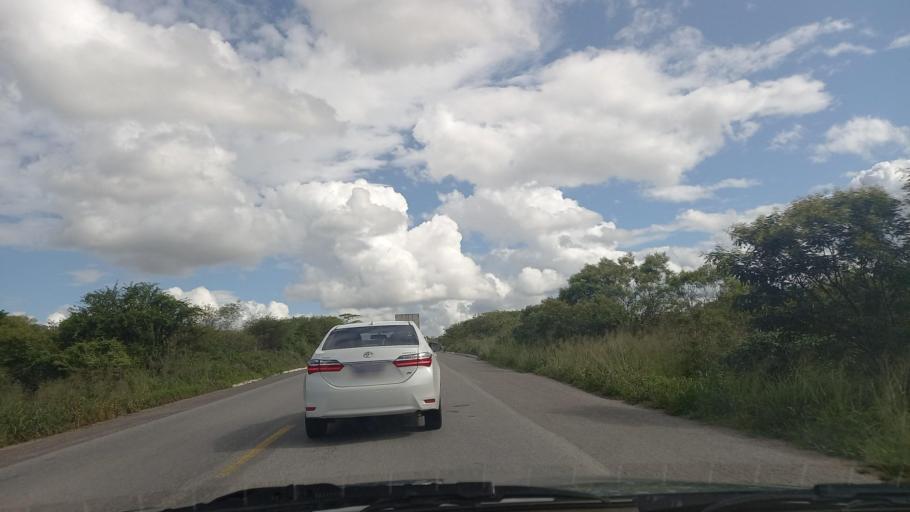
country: BR
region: Pernambuco
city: Garanhuns
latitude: -8.8152
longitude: -36.4458
